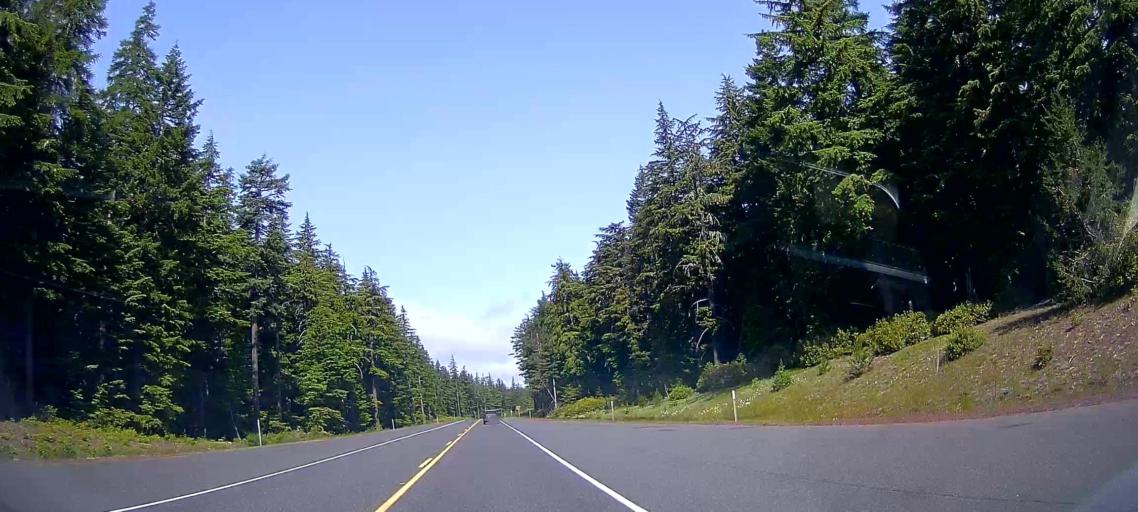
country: US
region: Oregon
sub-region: Clackamas County
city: Mount Hood Village
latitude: 45.1902
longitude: -121.6839
